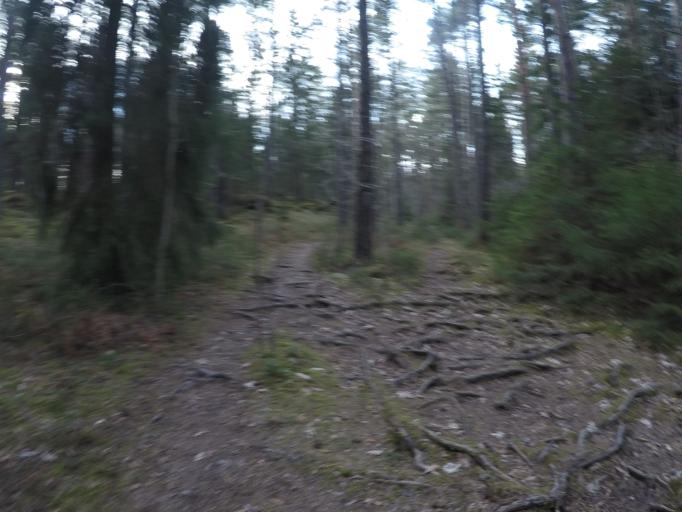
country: SE
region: Soedermanland
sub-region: Eskilstuna Kommun
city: Torshalla
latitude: 59.4309
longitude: 16.5031
